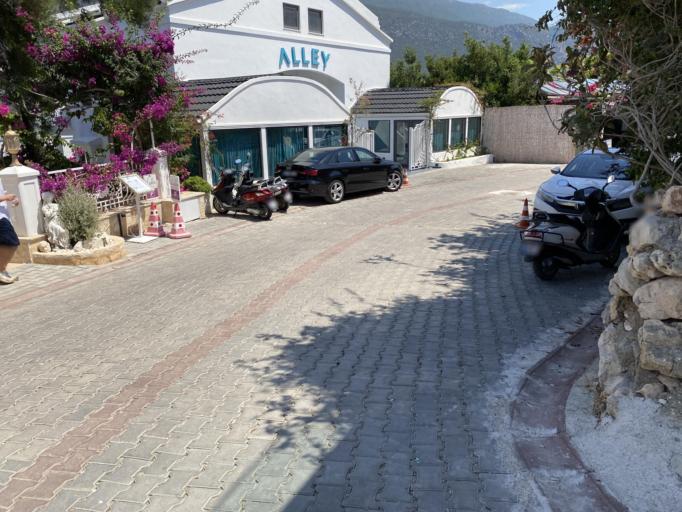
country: TR
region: Antalya
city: Kas
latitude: 36.1939
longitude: 29.5936
